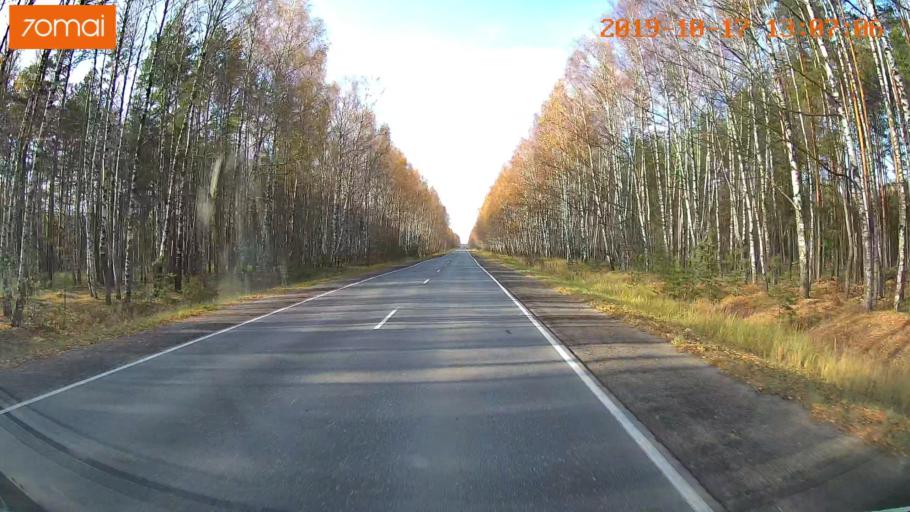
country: RU
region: Rjazan
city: Syntul
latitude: 54.9798
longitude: 41.2985
